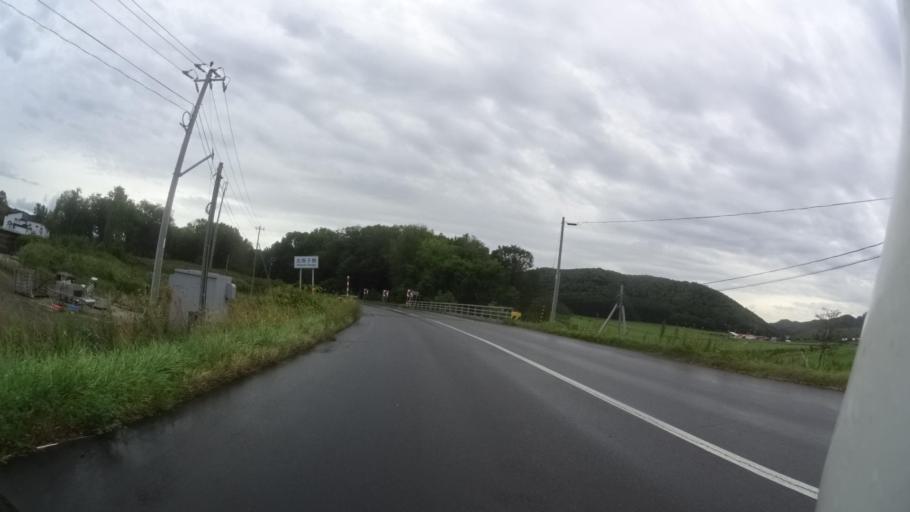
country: JP
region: Hokkaido
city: Kitami
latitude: 44.1127
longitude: 143.7220
